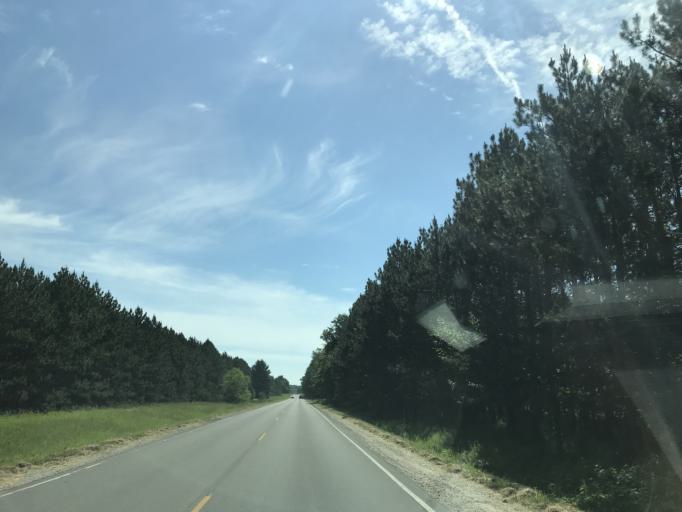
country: US
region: Michigan
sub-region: Grand Traverse County
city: Traverse City
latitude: 44.6544
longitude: -85.7158
